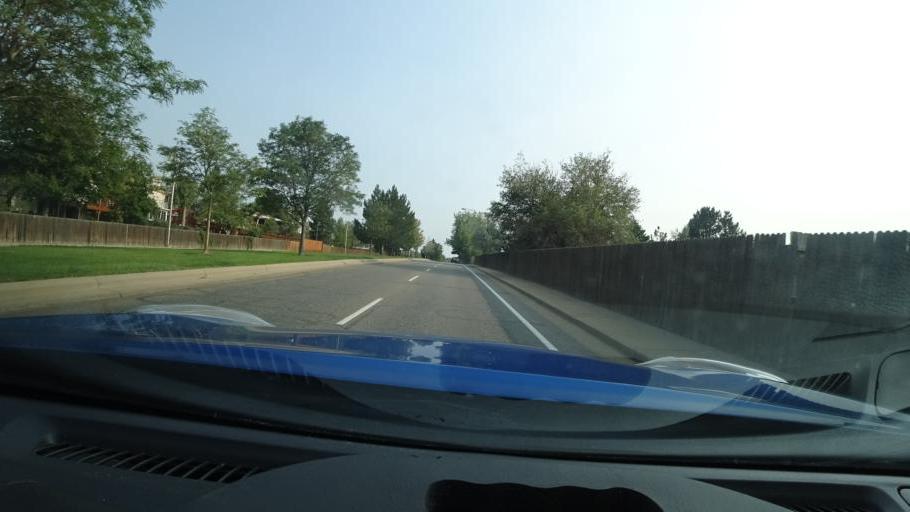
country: US
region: Colorado
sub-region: Adams County
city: Aurora
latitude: 39.6666
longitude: -104.7912
